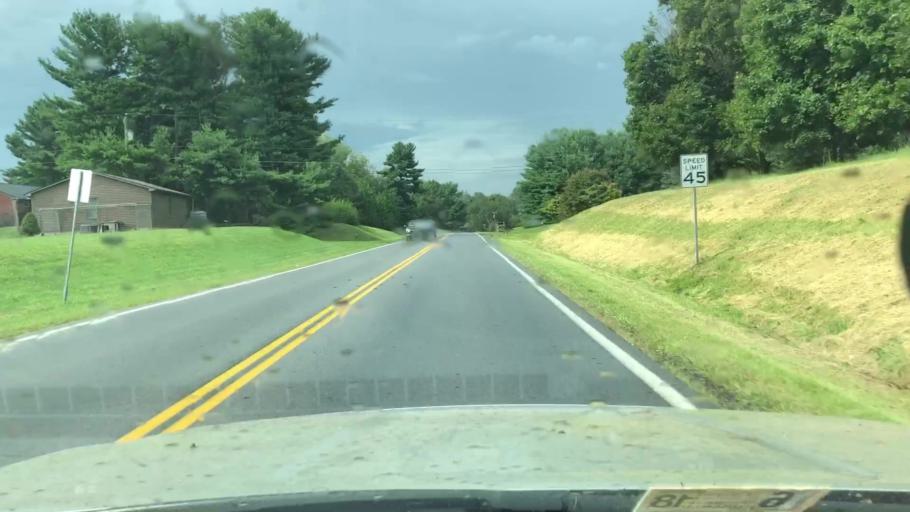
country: US
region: Virginia
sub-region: City of Waynesboro
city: Waynesboro
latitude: 38.0853
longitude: -78.9011
